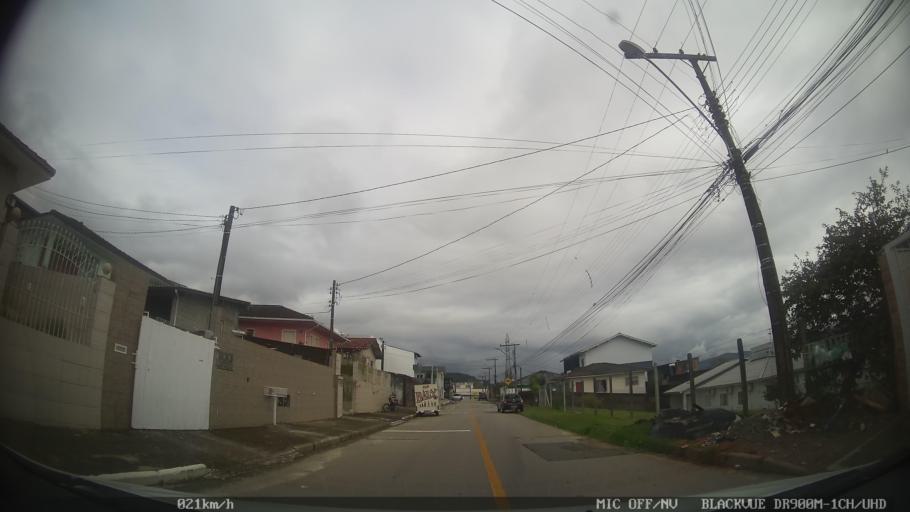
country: BR
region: Santa Catarina
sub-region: Sao Jose
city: Campinas
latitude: -27.5650
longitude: -48.6324
